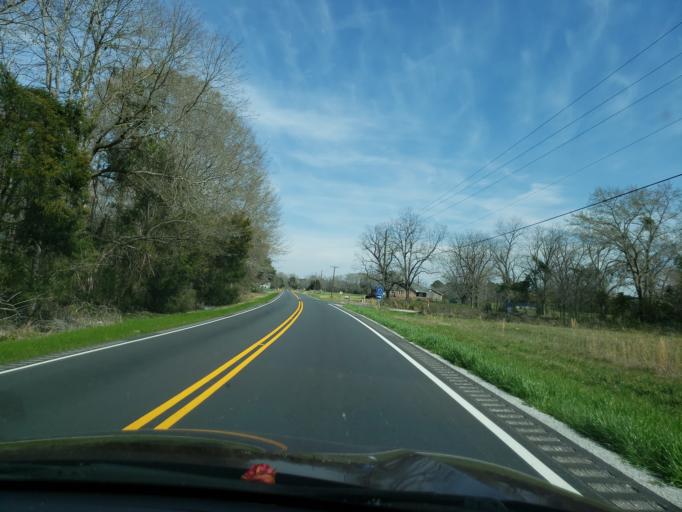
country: US
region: Alabama
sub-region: Elmore County
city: Tallassee
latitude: 32.5598
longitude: -85.7904
